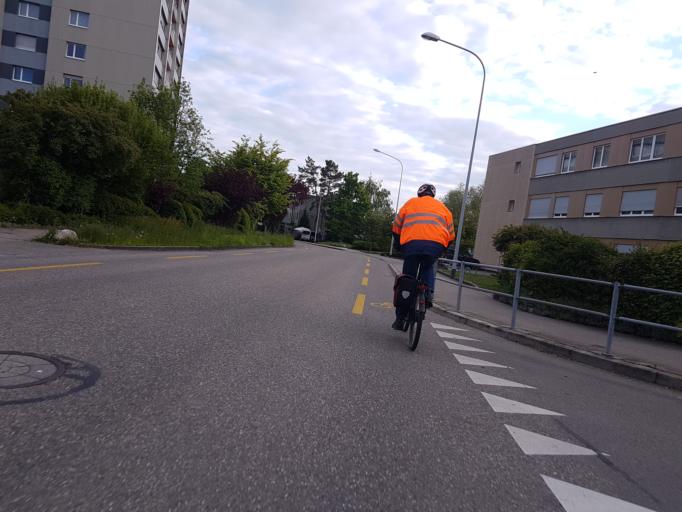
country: CH
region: Bern
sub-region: Biel/Bienne District
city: Nidau
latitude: 47.1209
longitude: 7.2362
